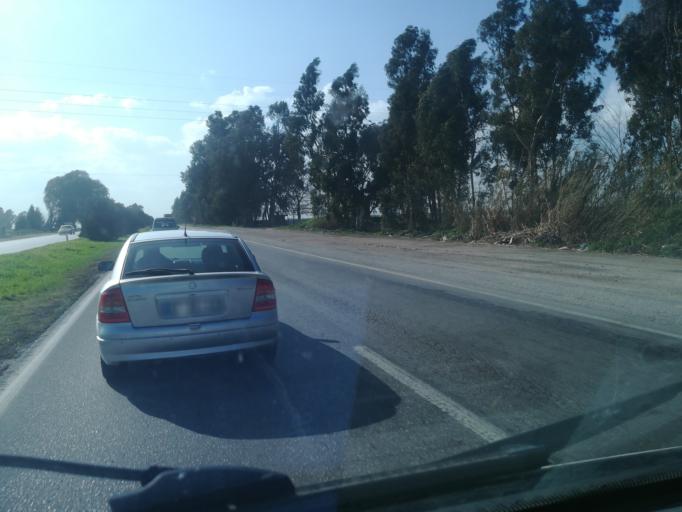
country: TR
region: Adana
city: Kosreli
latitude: 37.0646
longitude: 35.9589
